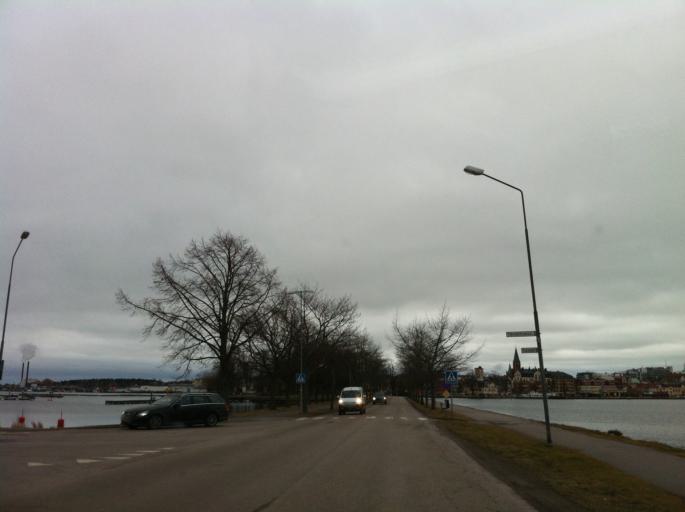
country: SE
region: Kalmar
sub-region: Vasterviks Kommun
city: Vaestervik
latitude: 57.8023
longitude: 16.6080
